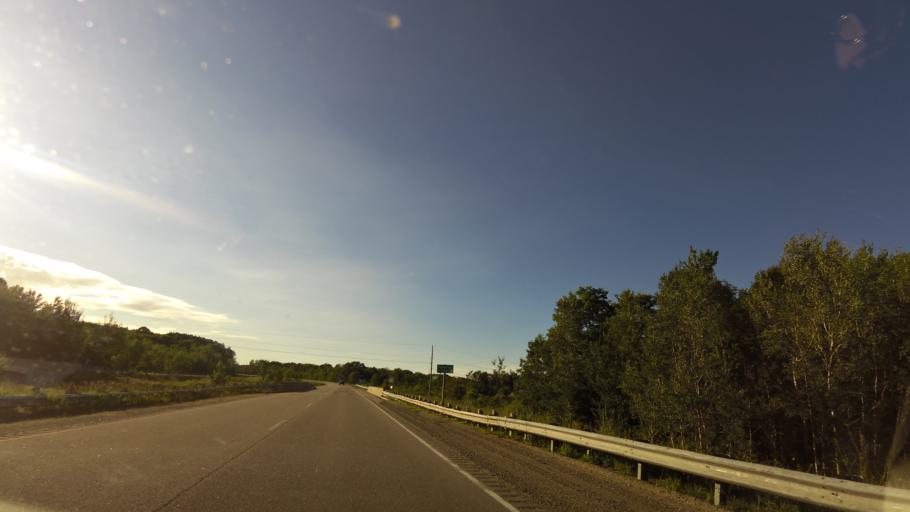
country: CA
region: Ontario
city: Midland
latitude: 44.7346
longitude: -79.6828
